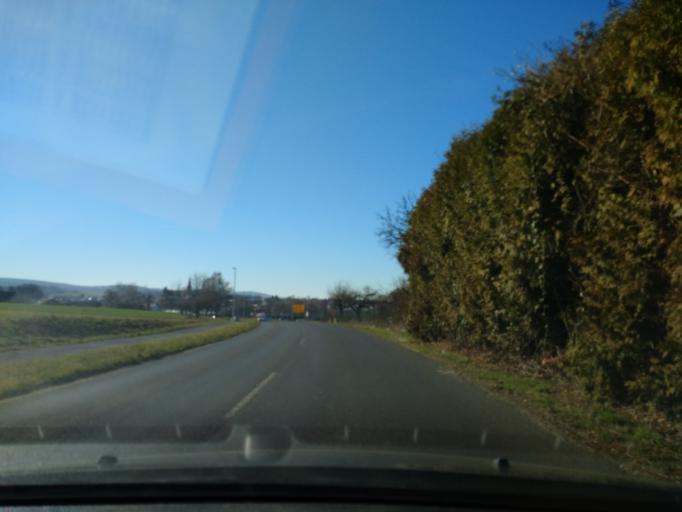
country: DE
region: Bavaria
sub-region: Regierungsbezirk Unterfranken
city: Geiselbach
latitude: 50.1505
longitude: 9.1431
